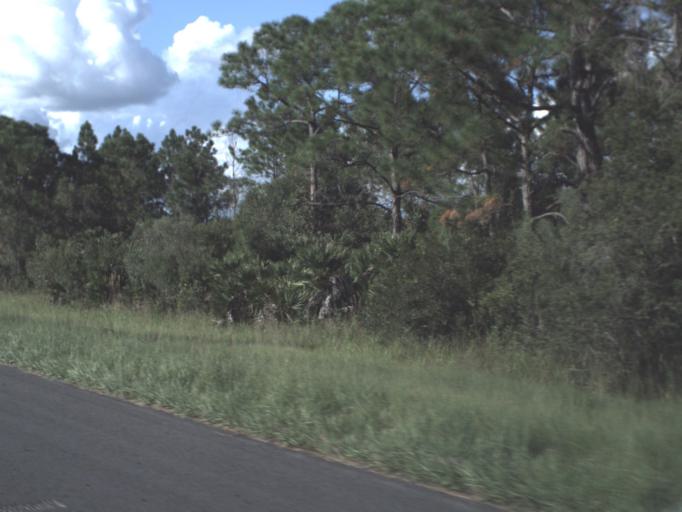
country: US
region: Florida
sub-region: Lee County
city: Suncoast Estates
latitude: 26.7853
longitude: -81.8994
